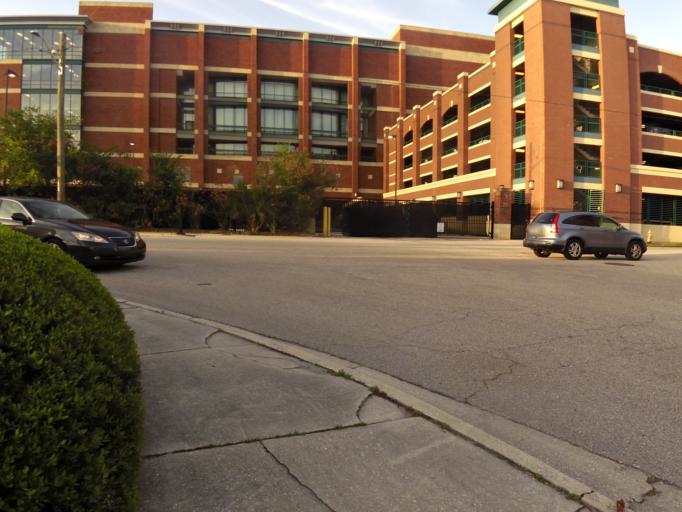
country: US
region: Florida
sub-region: Duval County
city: Jacksonville
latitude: 30.3247
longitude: -81.6455
